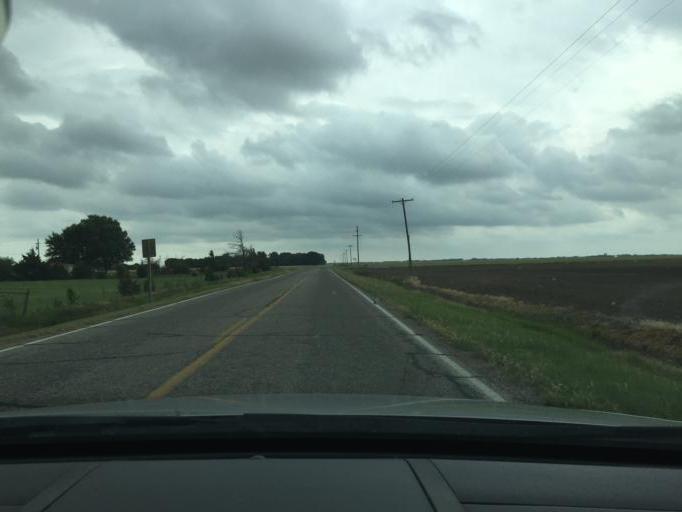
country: US
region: Kansas
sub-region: Reno County
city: South Hutchinson
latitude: 37.9701
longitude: -98.0157
